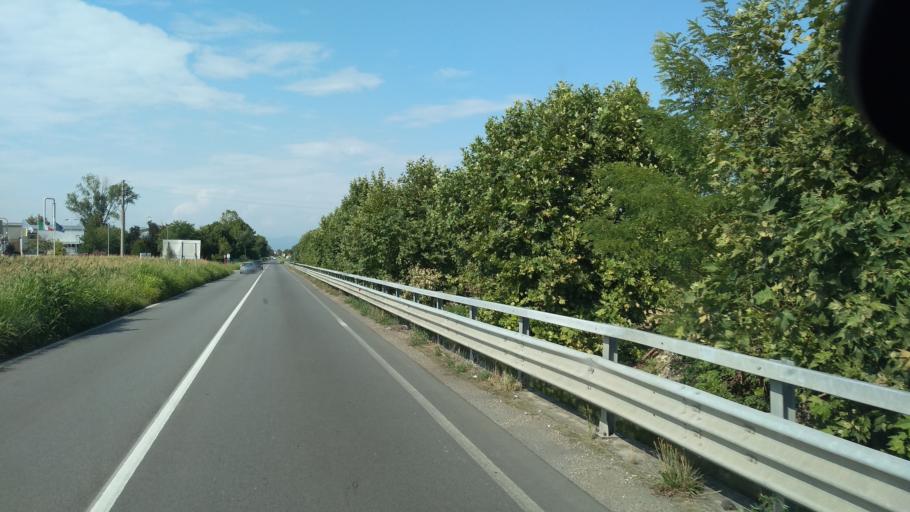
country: IT
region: Lombardy
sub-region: Provincia di Bergamo
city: Castel Rozzone
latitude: 45.5531
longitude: 9.6053
